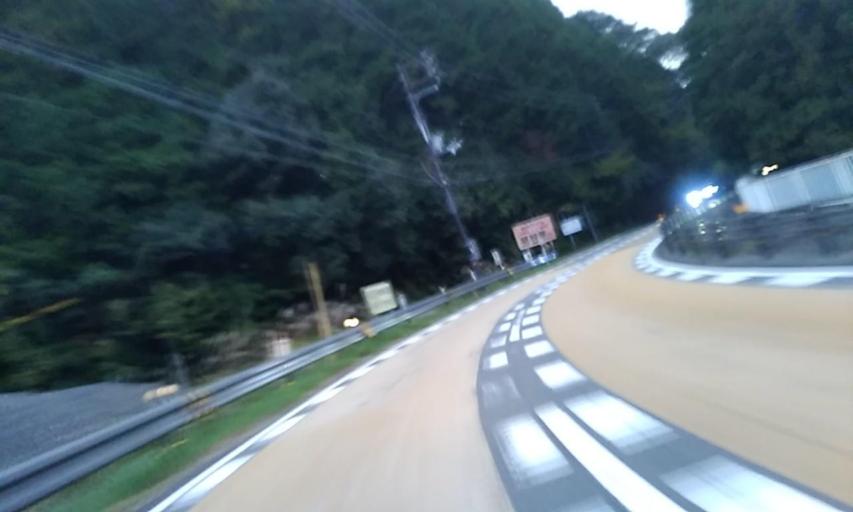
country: JP
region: Wakayama
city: Shingu
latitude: 33.7352
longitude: 135.9406
